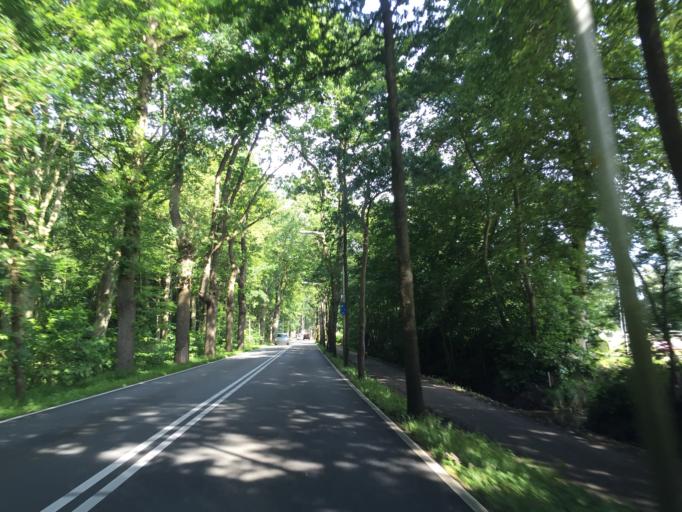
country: NL
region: South Holland
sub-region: Gemeente Wassenaar
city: Wassenaar
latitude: 52.1522
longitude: 4.3864
